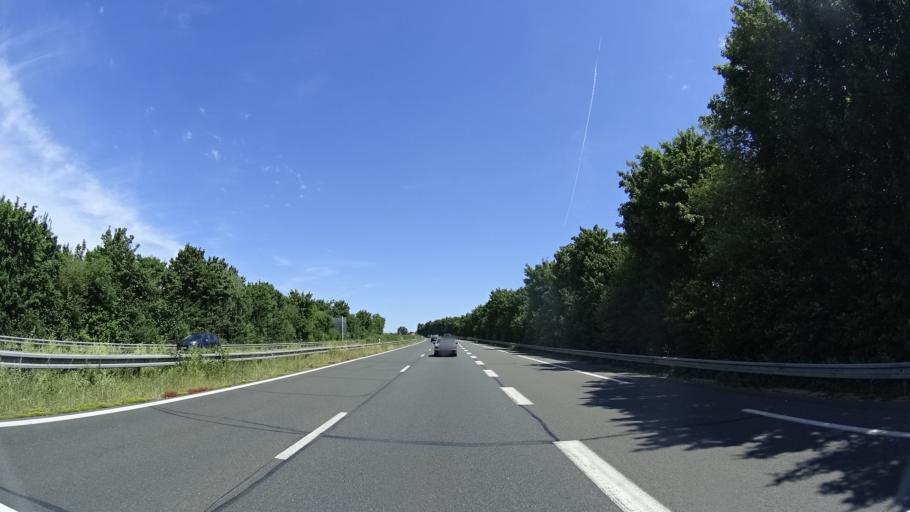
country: FR
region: Pays de la Loire
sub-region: Departement de Maine-et-Loire
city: Beaucouze
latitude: 47.5021
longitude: -0.6201
